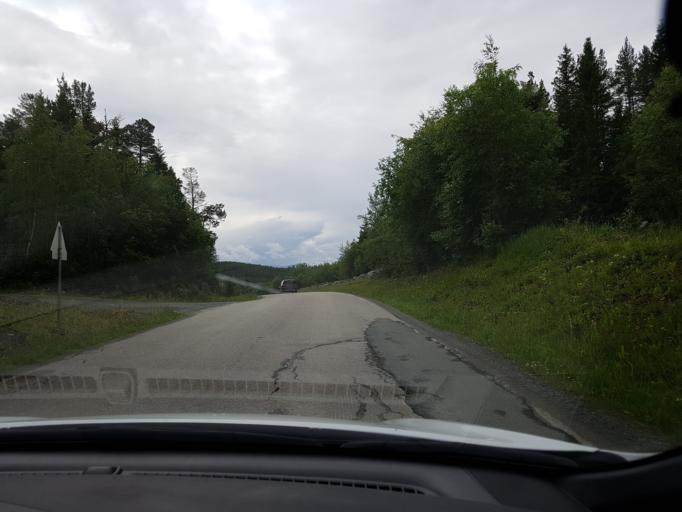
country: NO
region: Nord-Trondelag
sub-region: Frosta
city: Frosta
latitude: 63.6036
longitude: 10.7344
